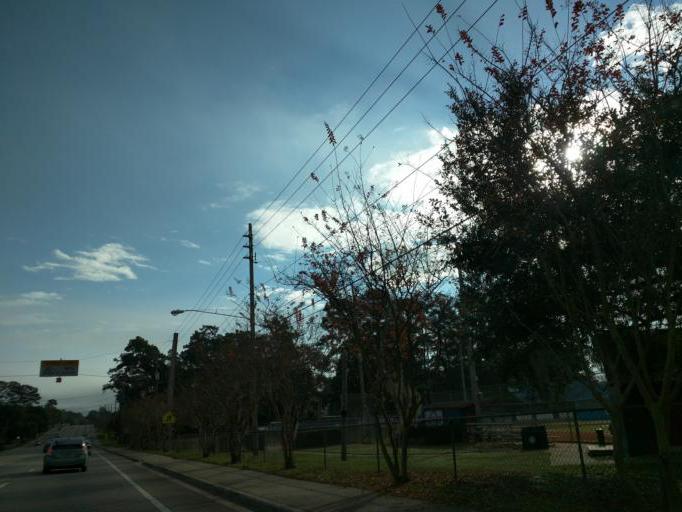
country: US
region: Florida
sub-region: Leon County
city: Tallahassee
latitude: 30.4636
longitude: -84.2911
